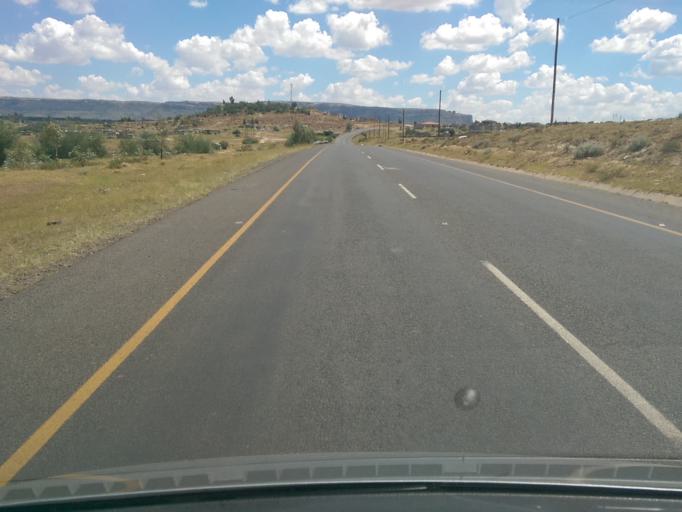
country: LS
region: Maseru
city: Maseru
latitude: -29.3944
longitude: 27.5273
